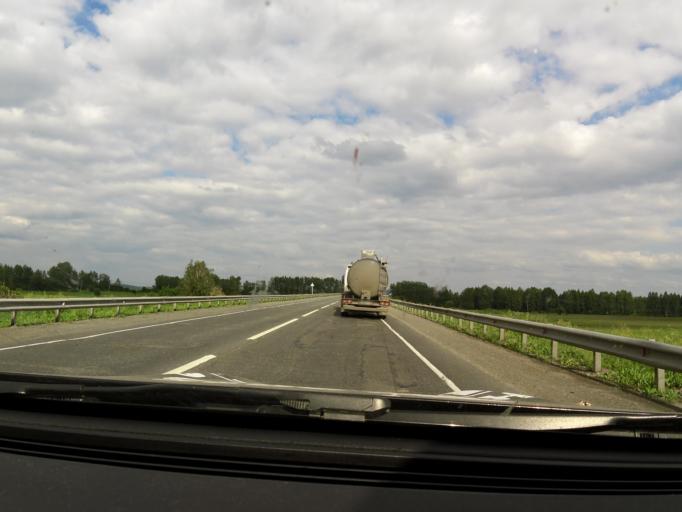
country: RU
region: Sverdlovsk
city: Druzhinino
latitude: 56.8105
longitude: 59.5082
